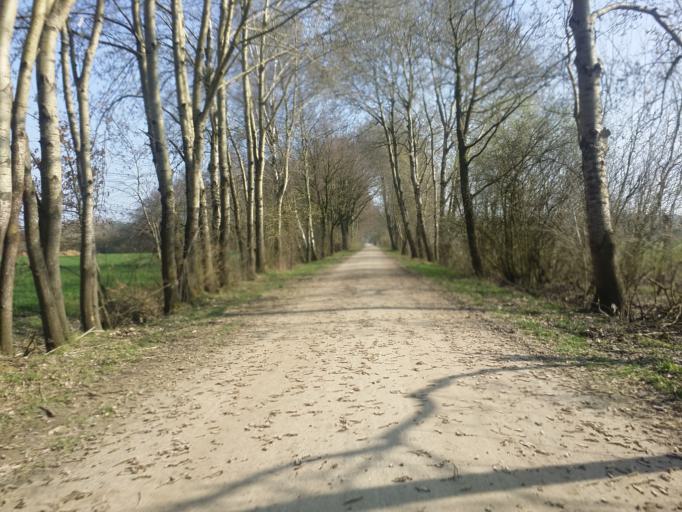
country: DE
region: Lower Saxony
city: Delmenhorst
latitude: 53.0145
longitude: 8.6689
